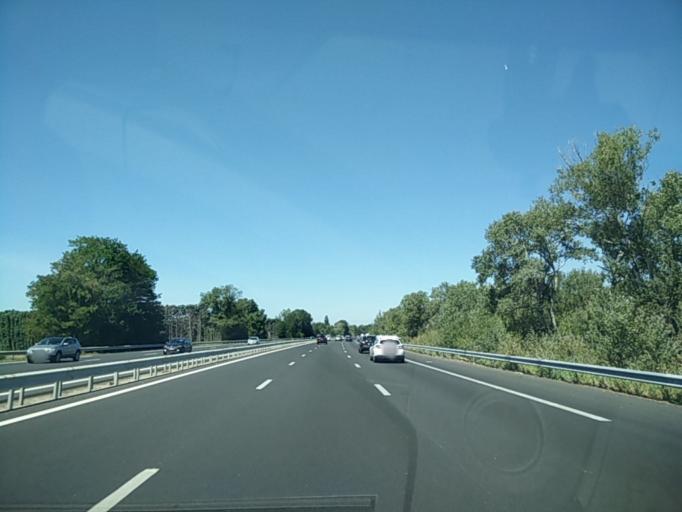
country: FR
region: Provence-Alpes-Cote d'Azur
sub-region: Departement du Vaucluse
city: Cavaillon
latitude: 43.8388
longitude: 4.9968
